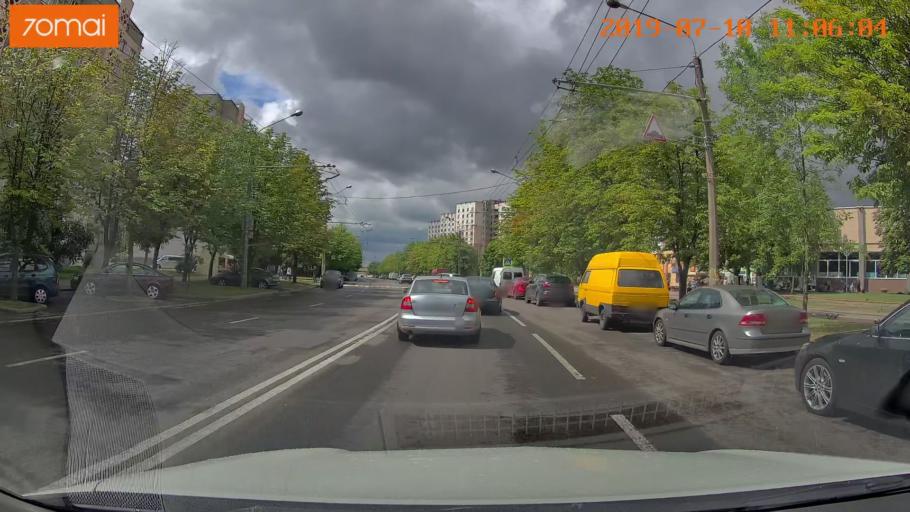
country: BY
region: Minsk
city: Syenitsa
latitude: 53.8513
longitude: 27.5473
